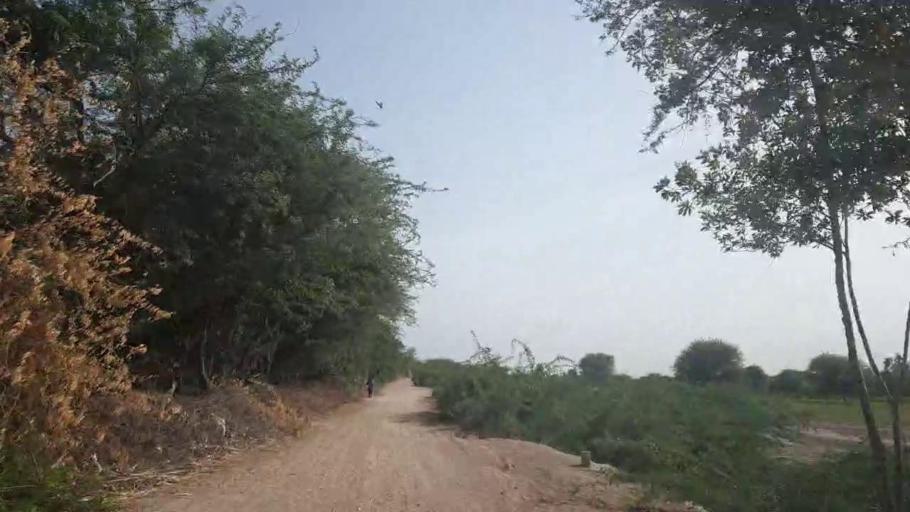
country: PK
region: Sindh
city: Tando Bago
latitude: 24.8038
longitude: 69.1859
